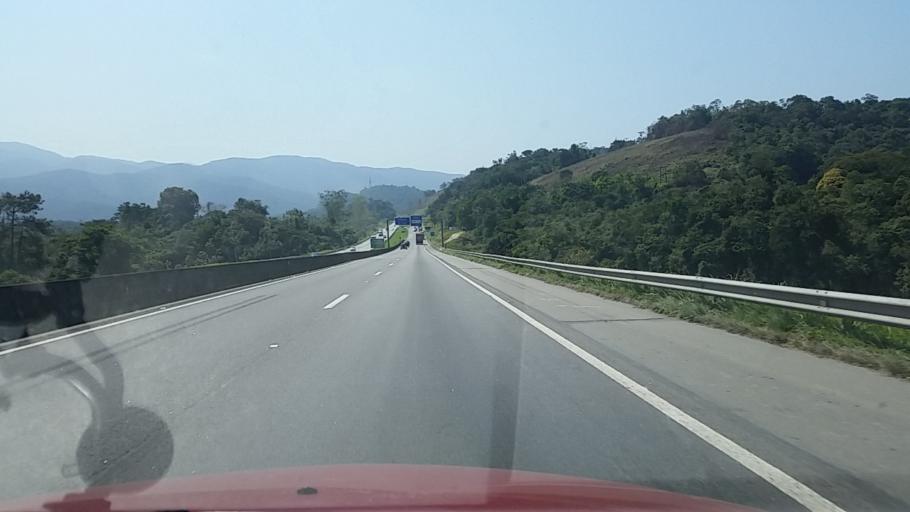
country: BR
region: Sao Paulo
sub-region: Miracatu
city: Miracatu
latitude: -24.1682
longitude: -47.3363
